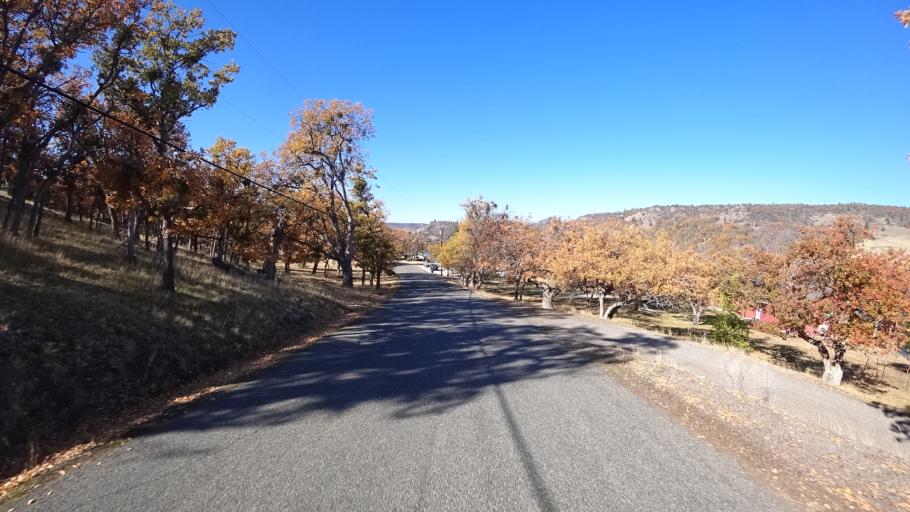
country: US
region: California
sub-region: Siskiyou County
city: Montague
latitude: 41.9796
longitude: -122.3139
